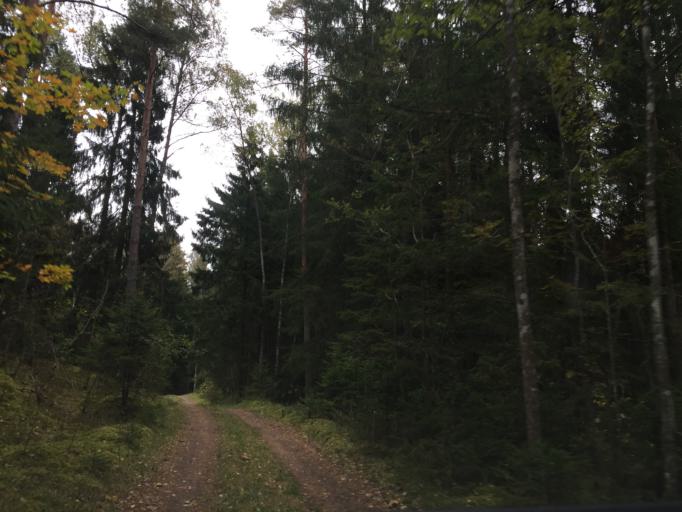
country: LV
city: Tireli
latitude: 56.8883
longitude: 23.5471
